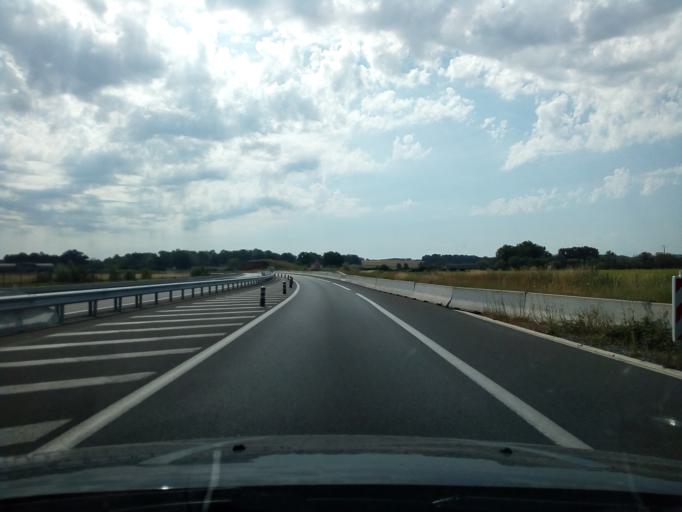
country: FR
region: Auvergne
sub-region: Departement de l'Allier
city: Varennes-sur-Allier
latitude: 46.3016
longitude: 3.4195
